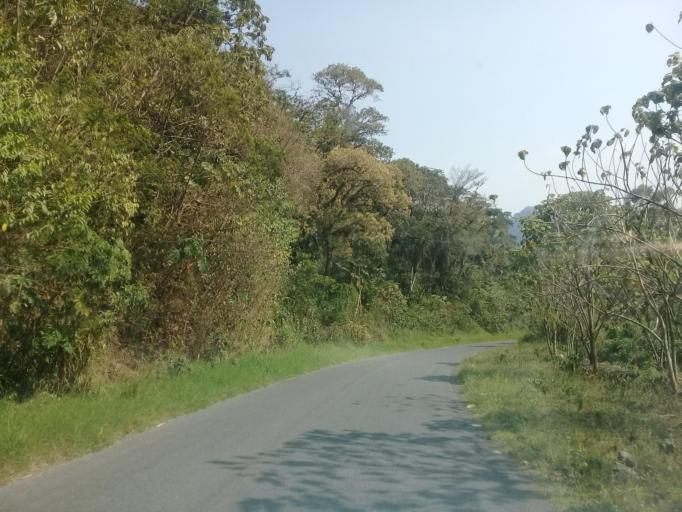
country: MX
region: Veracruz
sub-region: Ixtaczoquitlan
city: Campo Chico
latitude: 18.8325
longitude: -97.0140
